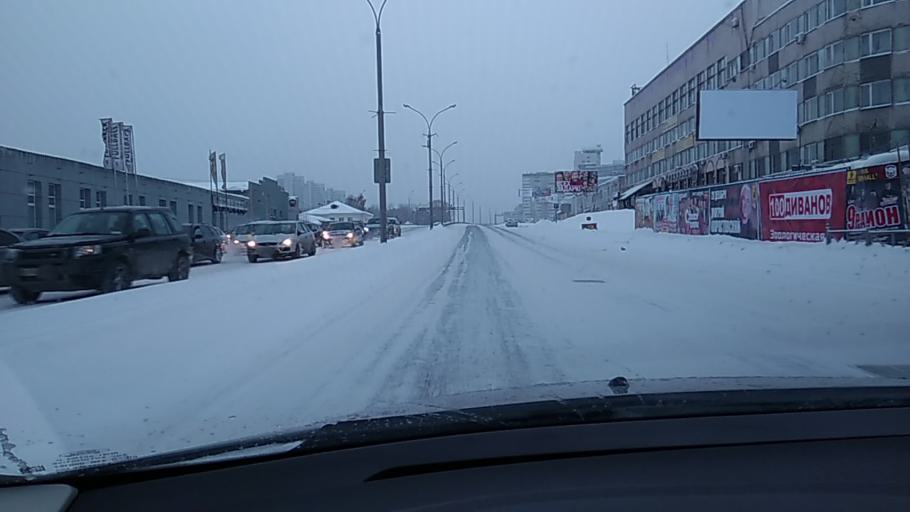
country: RU
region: Sverdlovsk
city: Yekaterinburg
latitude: 56.8253
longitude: 60.5667
